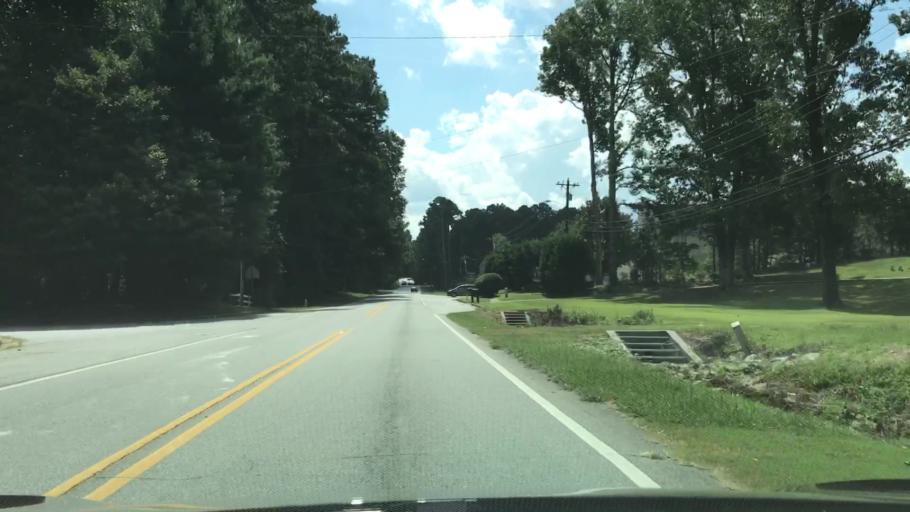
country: US
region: Georgia
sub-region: Gwinnett County
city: Lawrenceville
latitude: 33.9469
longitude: -84.0637
